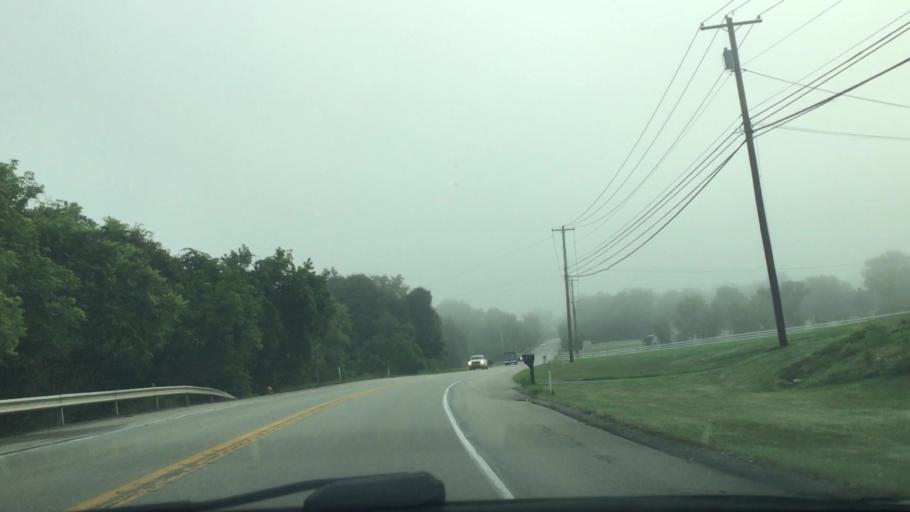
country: US
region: Pennsylvania
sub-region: Washington County
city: Canonsburg
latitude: 40.1970
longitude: -80.1333
